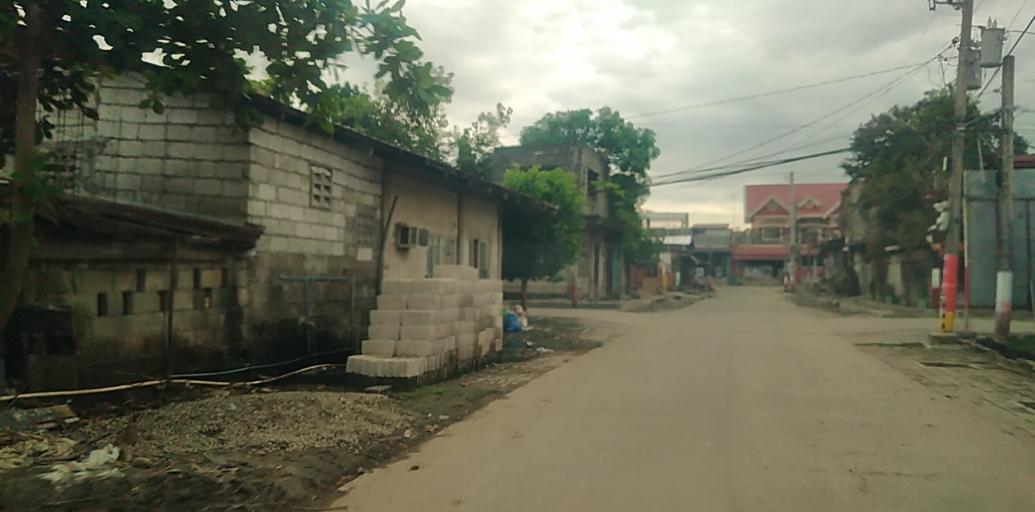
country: PH
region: Central Luzon
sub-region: Province of Pampanga
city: Pau
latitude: 15.0048
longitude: 120.7073
